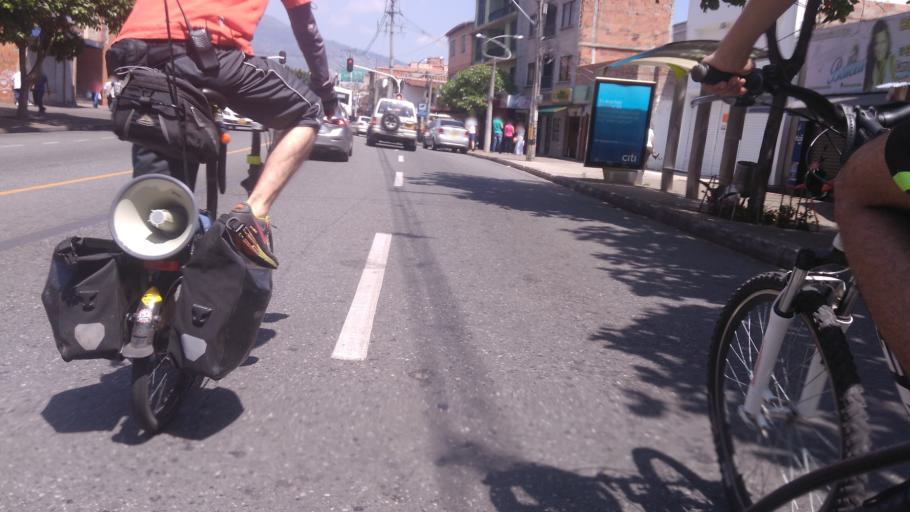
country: CO
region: Antioquia
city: Medellin
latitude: 6.2298
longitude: -75.5961
